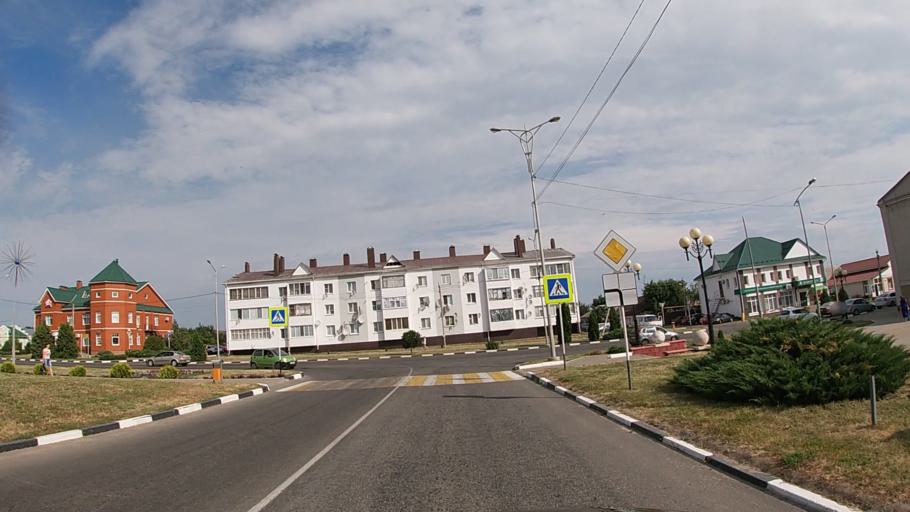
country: RU
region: Belgorod
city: Krasnaya Yaruga
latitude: 50.8022
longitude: 35.6595
